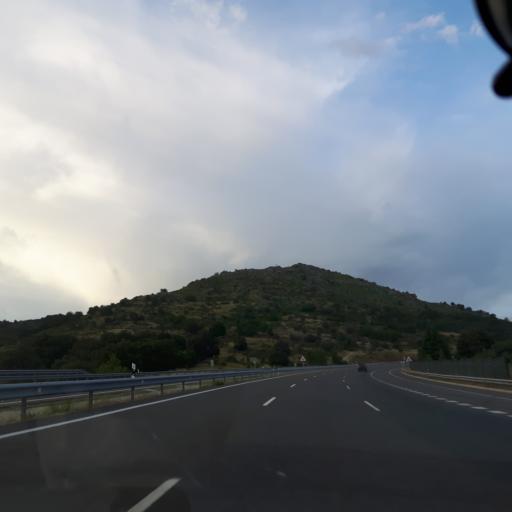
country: ES
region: Castille and Leon
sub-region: Provincia de Salamanca
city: Fresnedoso
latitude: 40.4331
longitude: -5.6948
